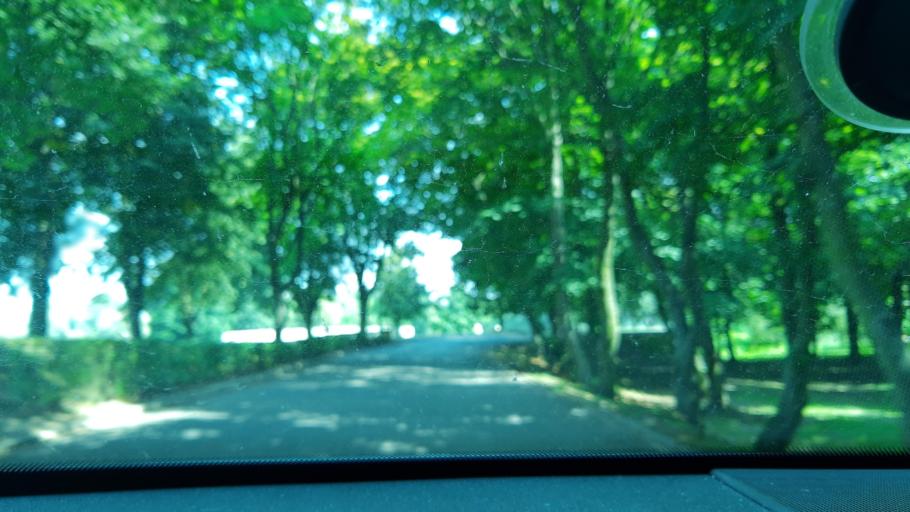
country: PL
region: Lodz Voivodeship
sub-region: Powiat sieradzki
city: Sieradz
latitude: 51.5997
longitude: 18.7414
